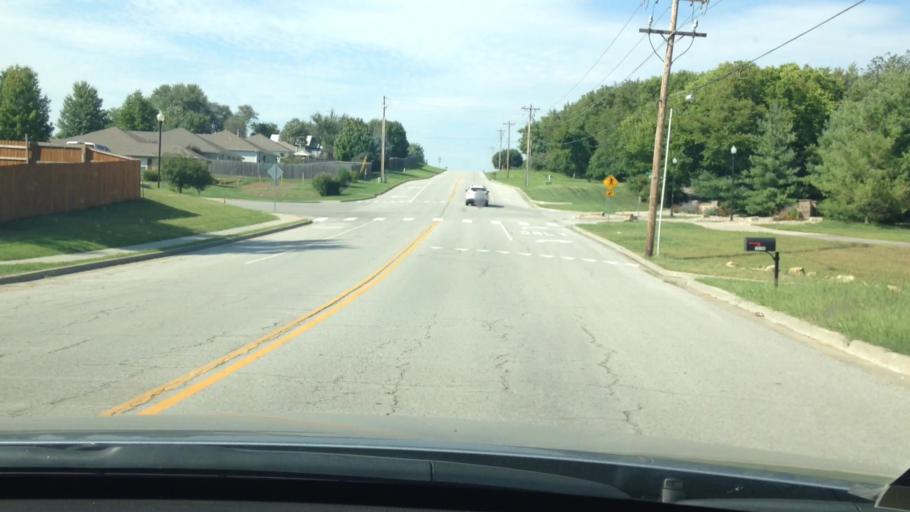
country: US
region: Missouri
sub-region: Platte County
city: Platte City
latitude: 39.3321
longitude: -94.7611
